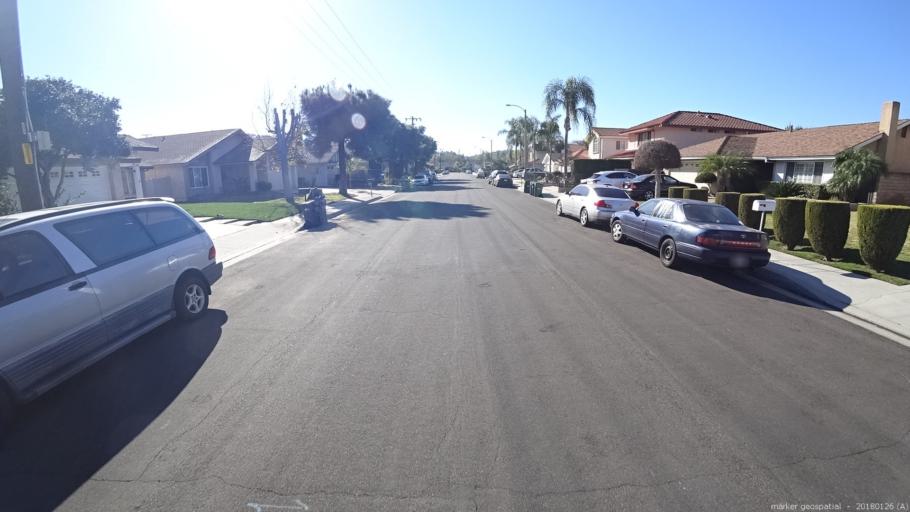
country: US
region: California
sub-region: Los Angeles County
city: Walnut
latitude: 34.0046
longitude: -117.8422
